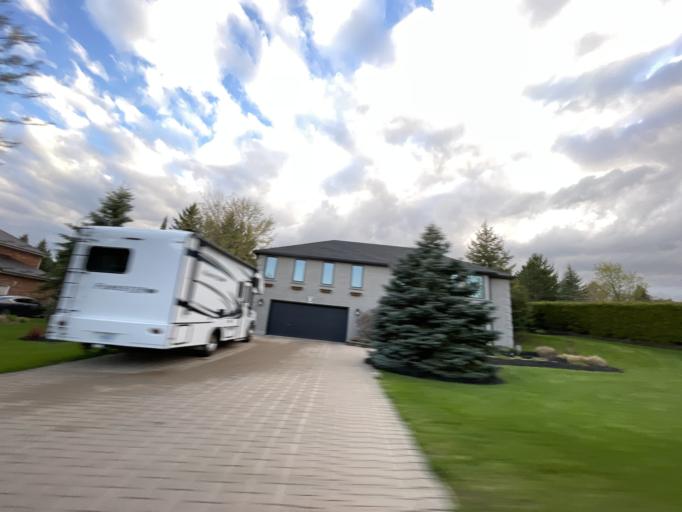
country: CA
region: Ontario
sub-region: Wellington County
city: Guelph
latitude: 43.5813
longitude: -80.2796
